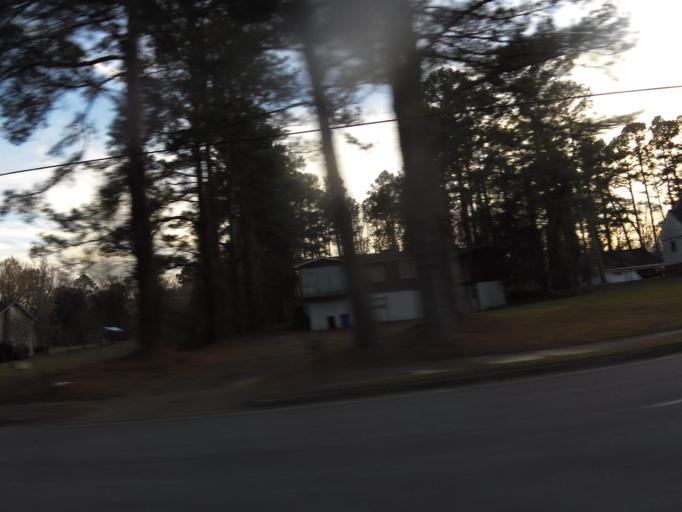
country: US
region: Virginia
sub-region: City of Franklin
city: Franklin
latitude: 36.6826
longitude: -76.9617
